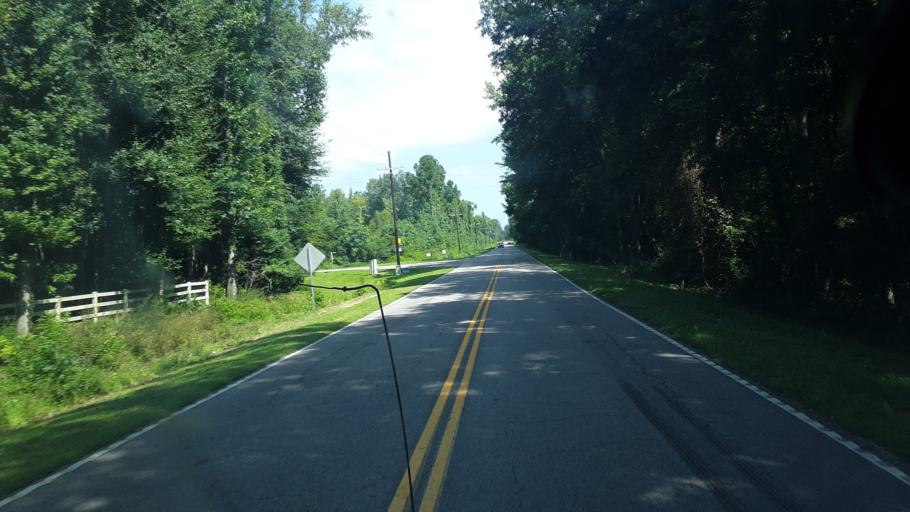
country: US
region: South Carolina
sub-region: Bamberg County
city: Bamberg
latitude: 33.2643
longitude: -81.0436
